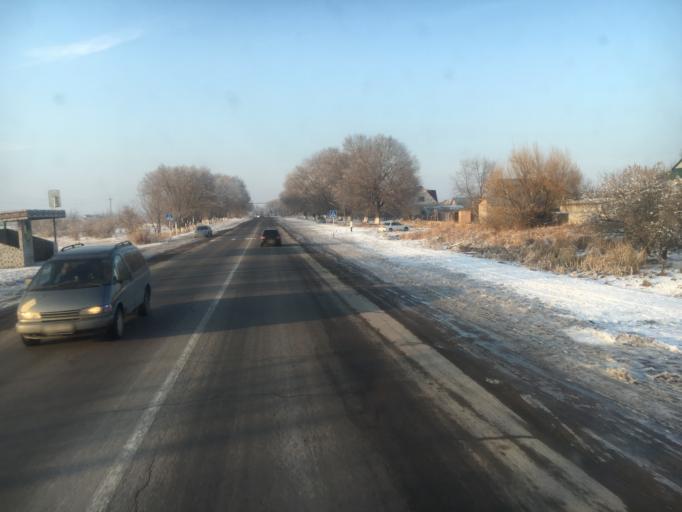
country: KZ
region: Almaty Oblysy
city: Burunday
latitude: 43.3371
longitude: 76.6598
